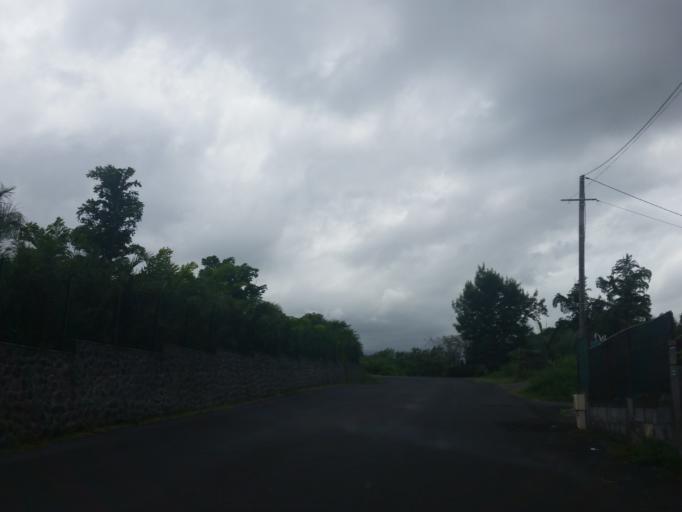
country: RE
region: Reunion
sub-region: Reunion
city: L'Entre-Deux
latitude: -21.2554
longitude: 55.4935
